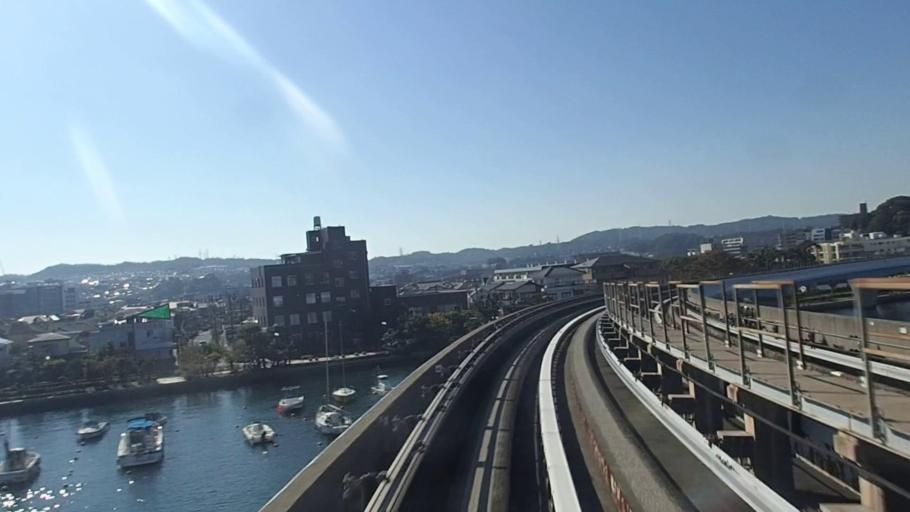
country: JP
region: Kanagawa
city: Yokosuka
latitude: 35.3290
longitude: 139.6272
